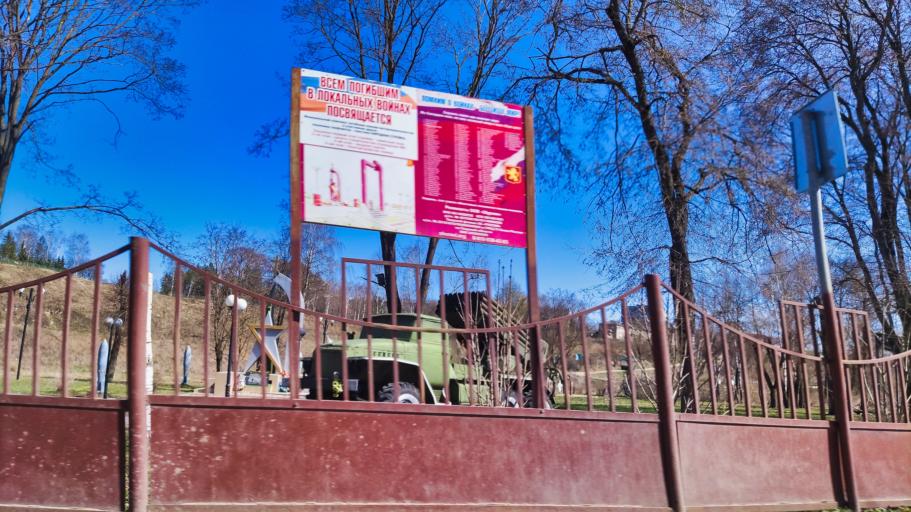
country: RU
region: Tverskaya
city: Rzhev
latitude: 56.2582
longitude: 34.3362
